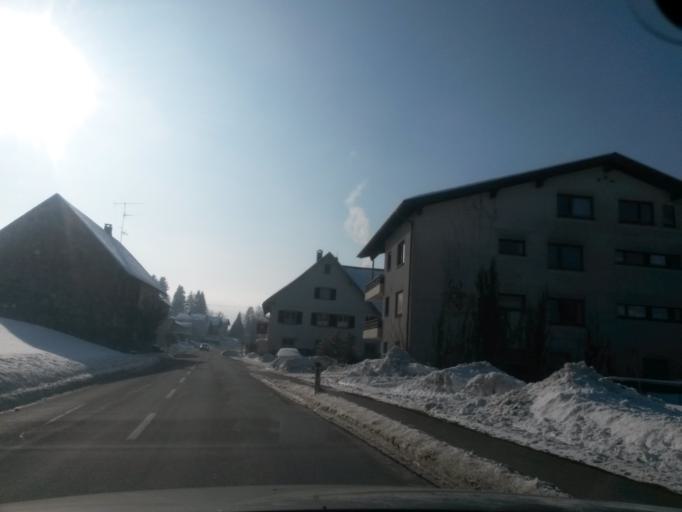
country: DE
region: Bavaria
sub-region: Swabia
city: Sigmarszell
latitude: 47.5752
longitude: 9.7728
